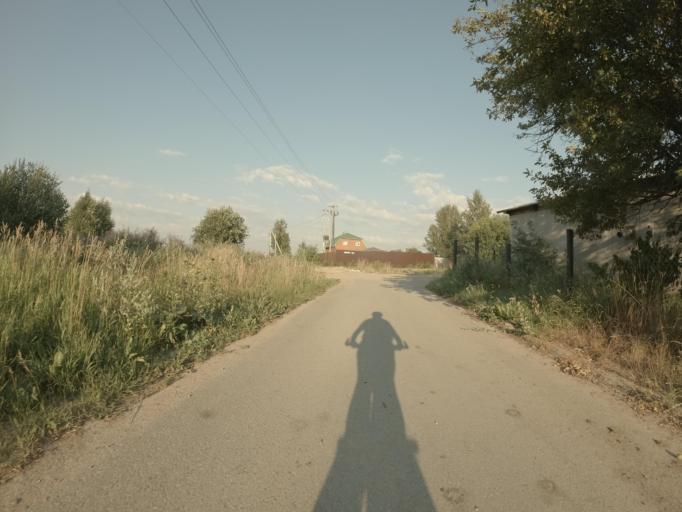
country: RU
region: Leningrad
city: Koltushi
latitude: 59.8906
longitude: 30.6976
